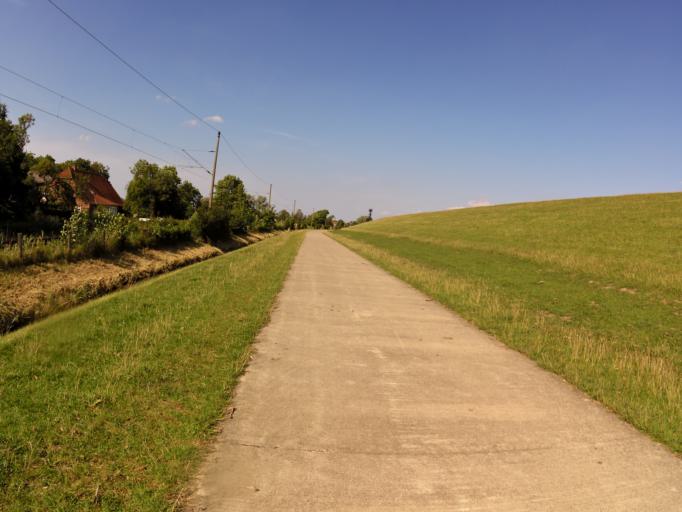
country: DE
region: Lower Saxony
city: Nordenham
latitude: 53.4607
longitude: 8.4750
